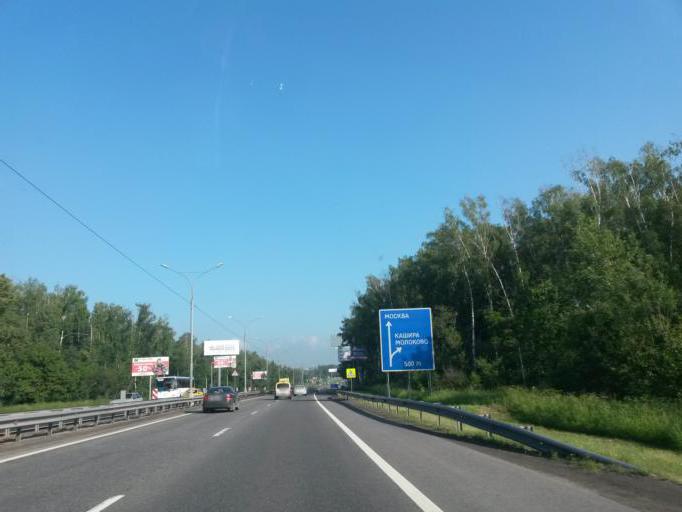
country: RU
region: Moskovskaya
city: Petrovskaya
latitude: 55.5534
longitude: 37.7847
